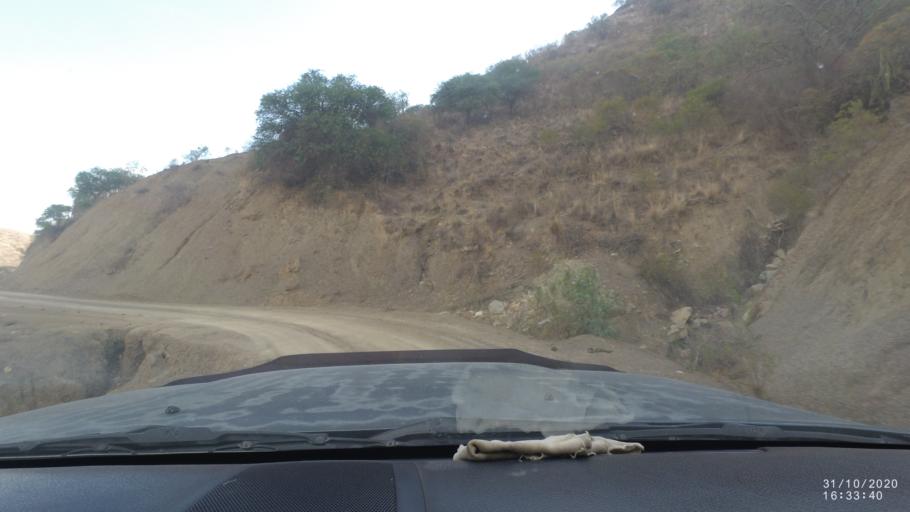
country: BO
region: Chuquisaca
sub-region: Provincia Zudanez
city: Mojocoya
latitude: -18.4437
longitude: -64.5849
